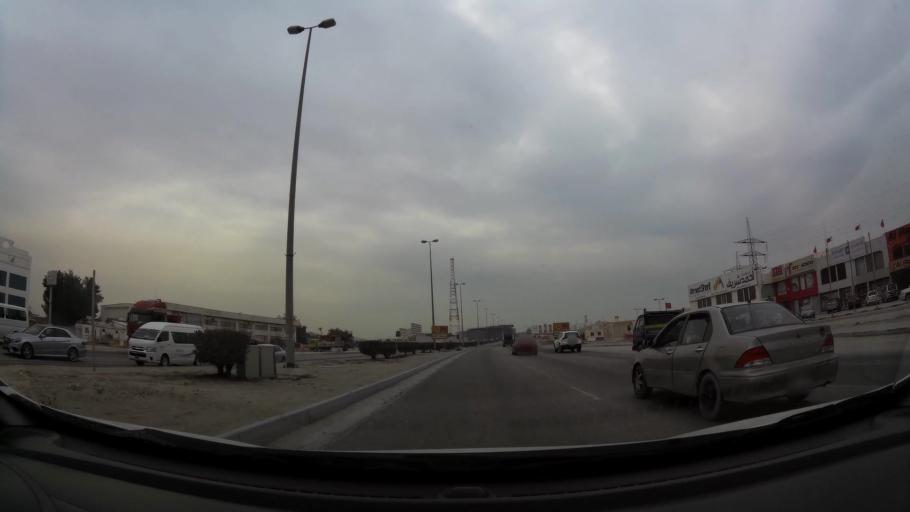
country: BH
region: Northern
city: Sitrah
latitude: 26.1268
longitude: 50.5960
